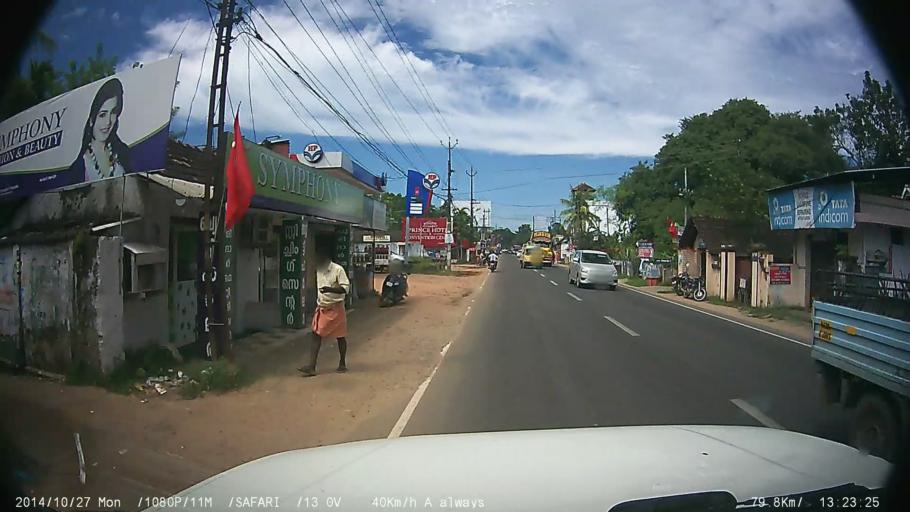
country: IN
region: Kerala
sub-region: Alappuzha
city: Alleppey
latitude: 9.5037
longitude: 76.3286
